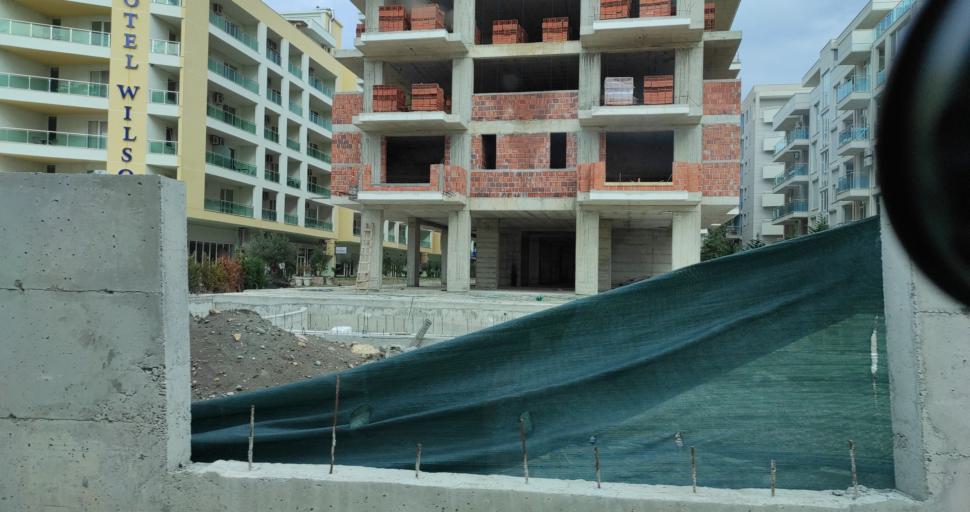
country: AL
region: Lezhe
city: Shengjin
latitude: 41.8058
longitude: 19.5998
